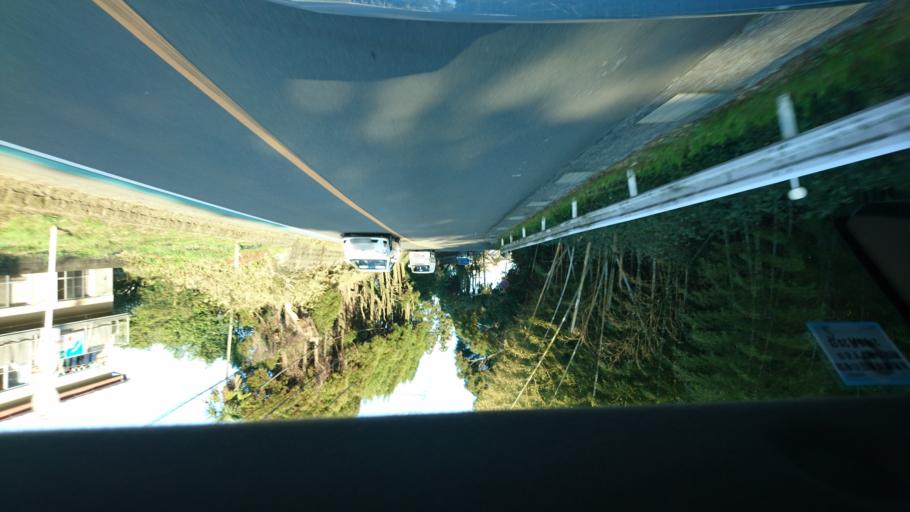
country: JP
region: Miyazaki
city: Miyazaki-shi
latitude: 31.8498
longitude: 131.3843
